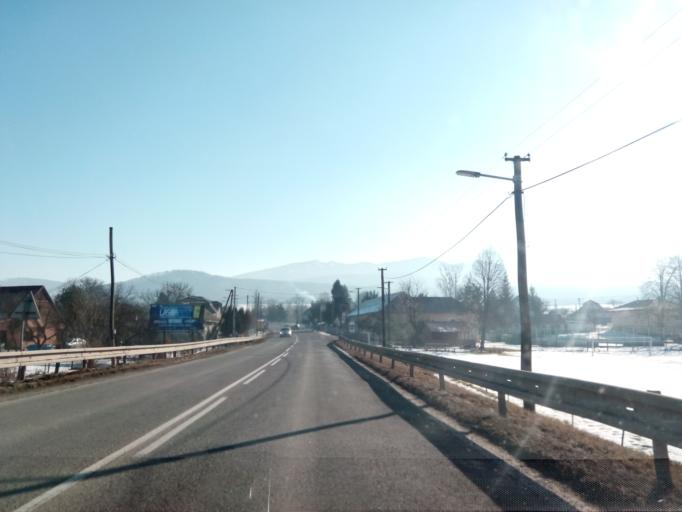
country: SK
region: Kosicky
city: Kosice
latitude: 48.7323
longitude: 21.4576
